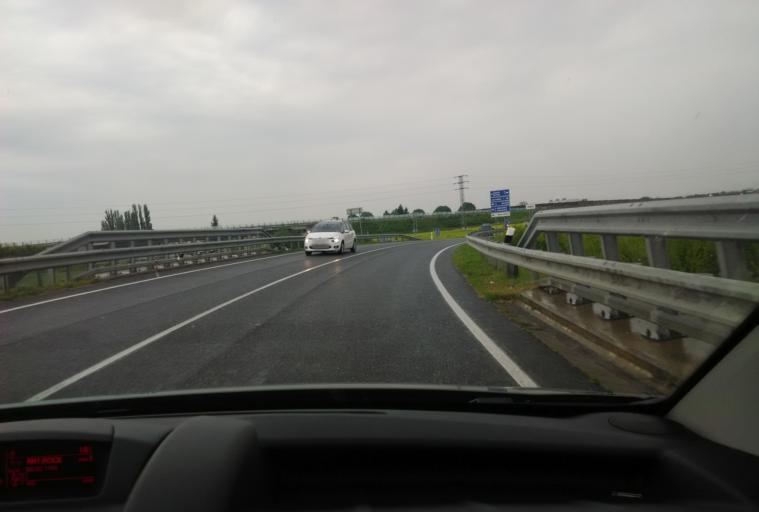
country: SK
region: Trnavsky
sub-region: Okres Trnava
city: Trnava
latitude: 48.3984
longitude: 17.6011
